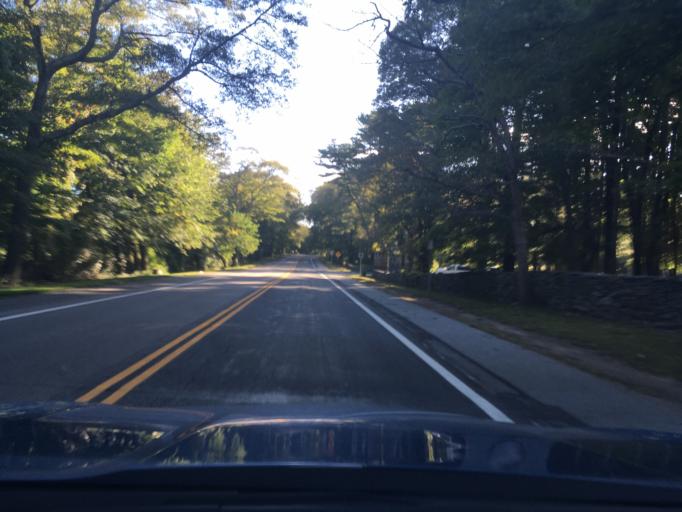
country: US
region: Rhode Island
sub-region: Kent County
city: East Greenwich
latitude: 41.6499
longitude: -71.4432
